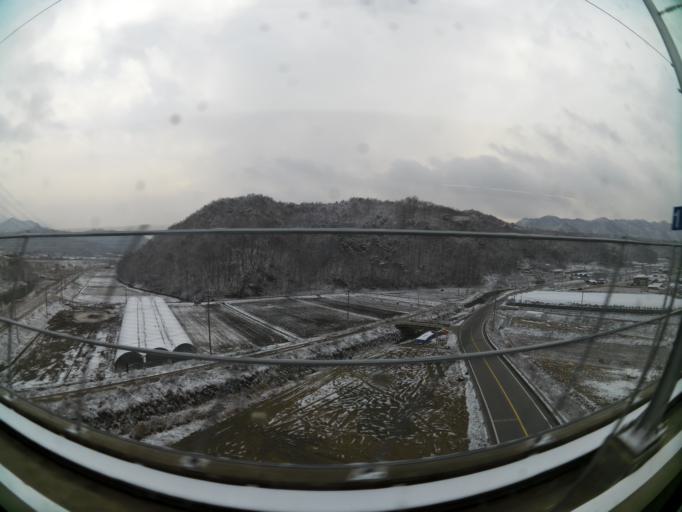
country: KR
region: Chungcheongbuk-do
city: Okcheon
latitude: 36.2631
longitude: 127.5683
